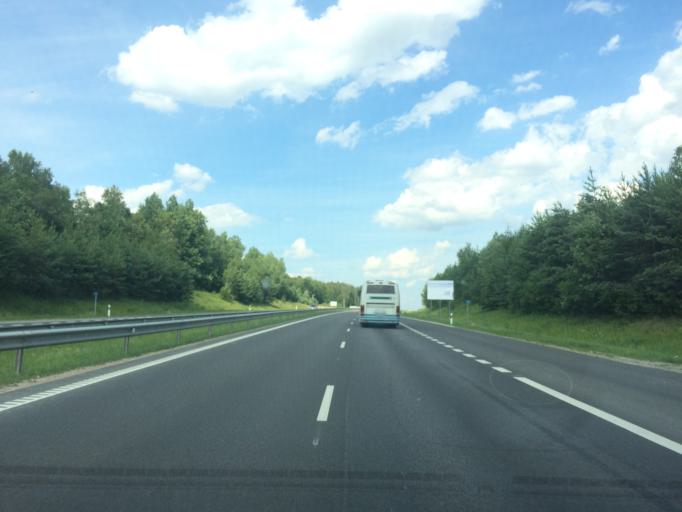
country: LT
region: Kauno apskritis
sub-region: Kauno rajonas
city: Karmelava
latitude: 54.9898
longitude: 24.1117
